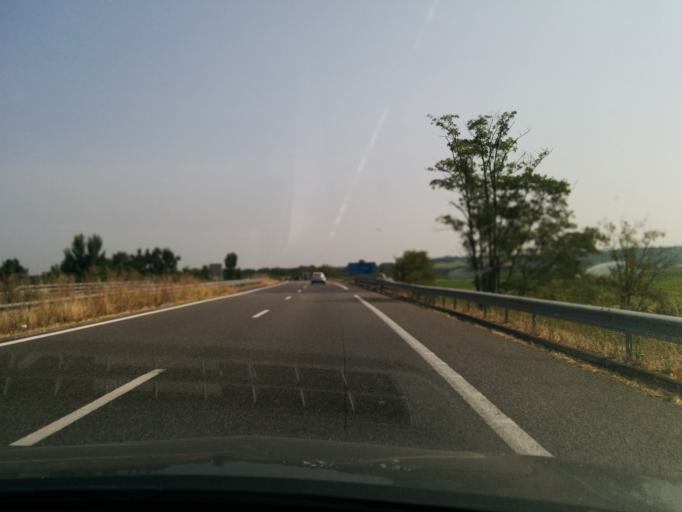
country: FR
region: Midi-Pyrenees
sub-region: Departement du Tarn
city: Saint-Sulpice-la-Pointe
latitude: 43.7651
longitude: 1.7198
